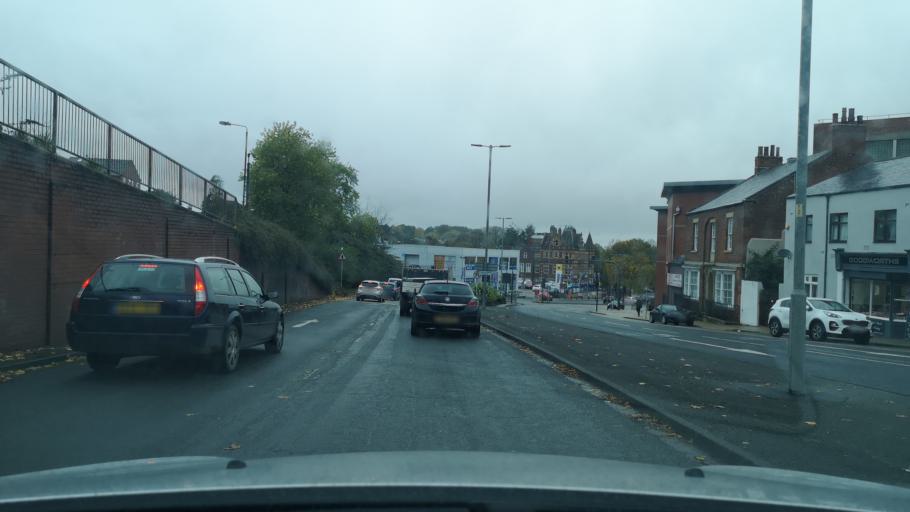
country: GB
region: England
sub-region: City and Borough of Wakefield
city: Pontefract
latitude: 53.6918
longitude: -1.3164
